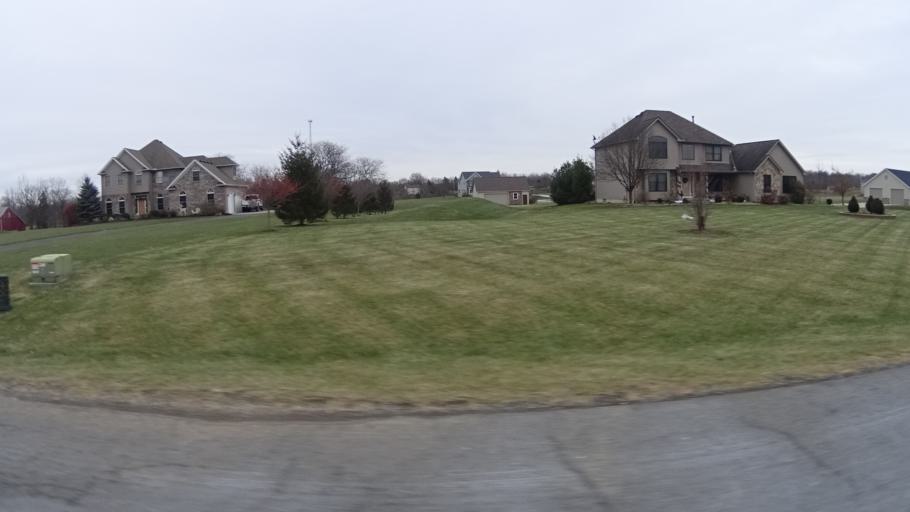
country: US
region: Ohio
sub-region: Lorain County
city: Grafton
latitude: 41.2623
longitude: -82.0480
